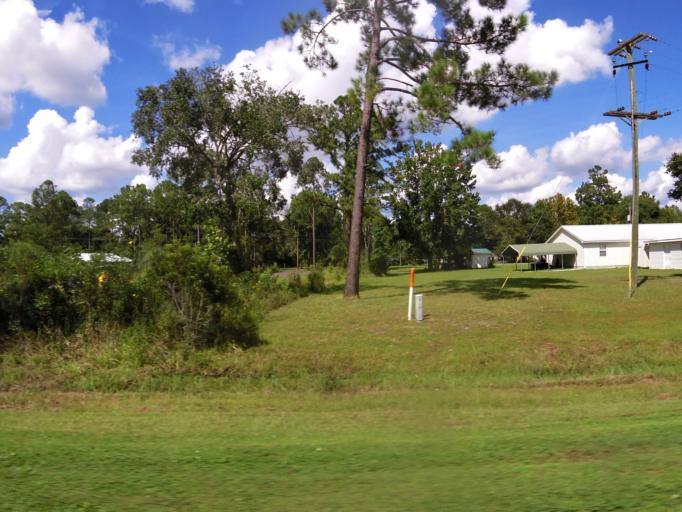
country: US
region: Georgia
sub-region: Clinch County
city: Homerville
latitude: 30.6850
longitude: -82.5669
